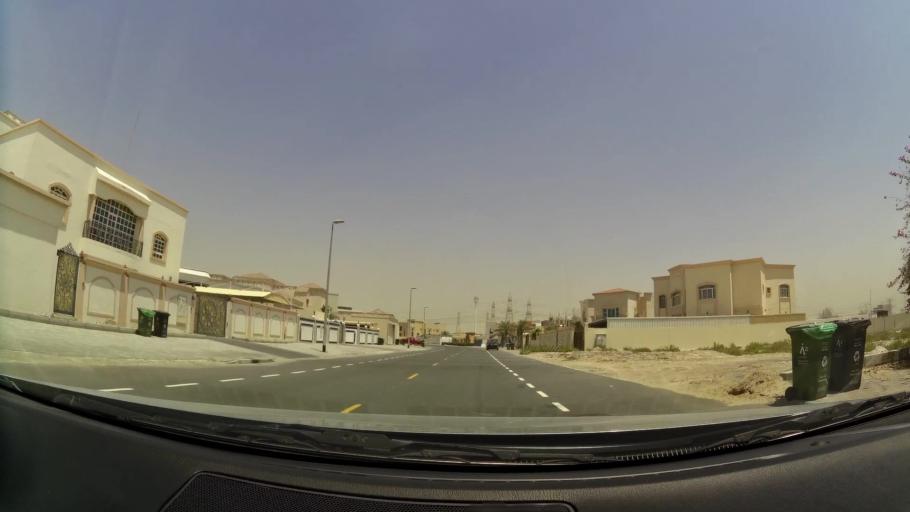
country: AE
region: Dubai
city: Dubai
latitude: 25.0828
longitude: 55.2056
